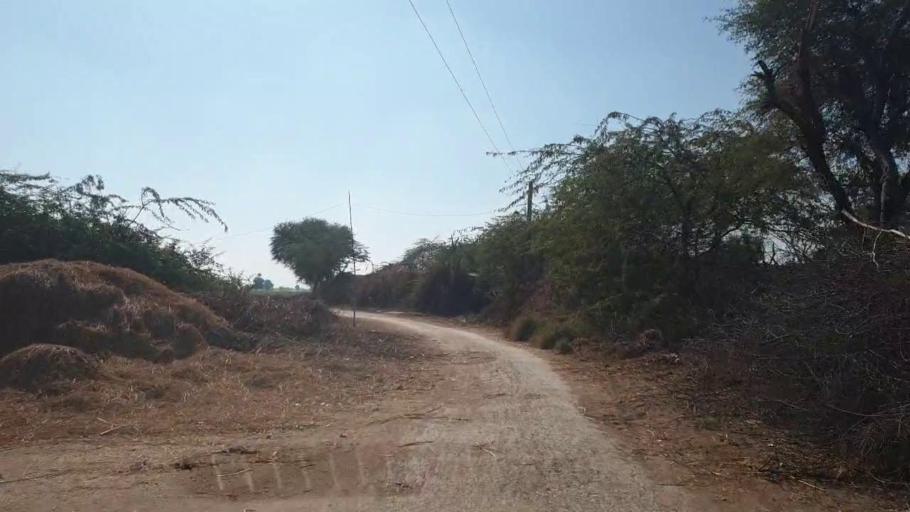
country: PK
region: Sindh
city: Shahpur Chakar
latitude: 26.1257
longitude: 68.6401
